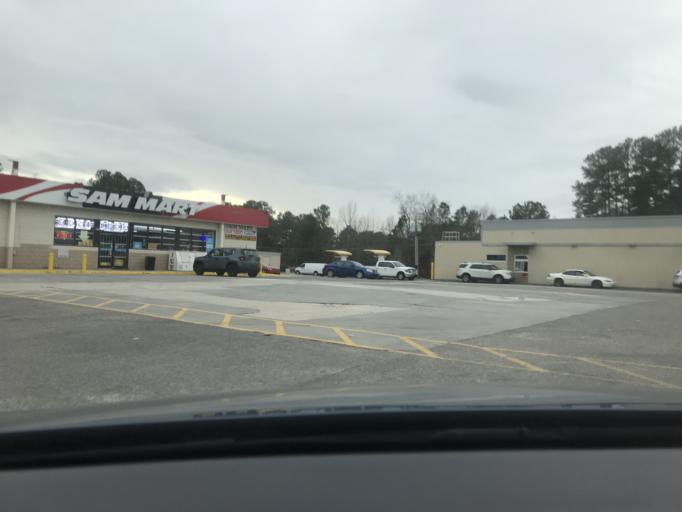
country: US
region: North Carolina
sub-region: Hoke County
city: Rockfish
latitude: 35.0374
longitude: -79.0064
